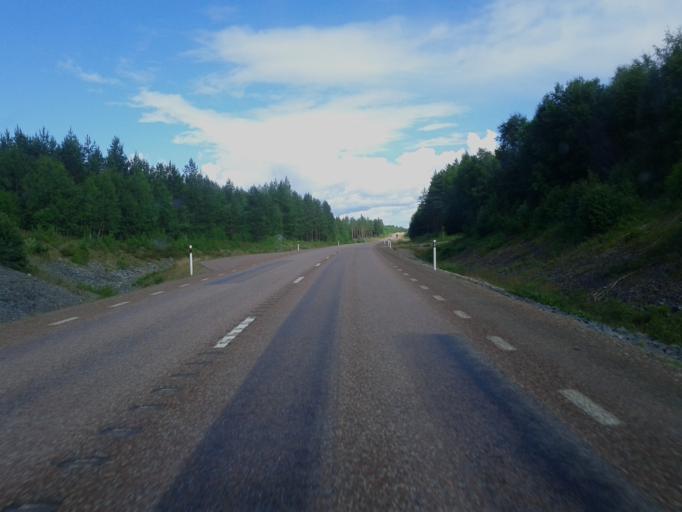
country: SE
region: Dalarna
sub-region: Rattviks Kommun
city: Raettvik
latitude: 60.8458
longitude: 15.1566
